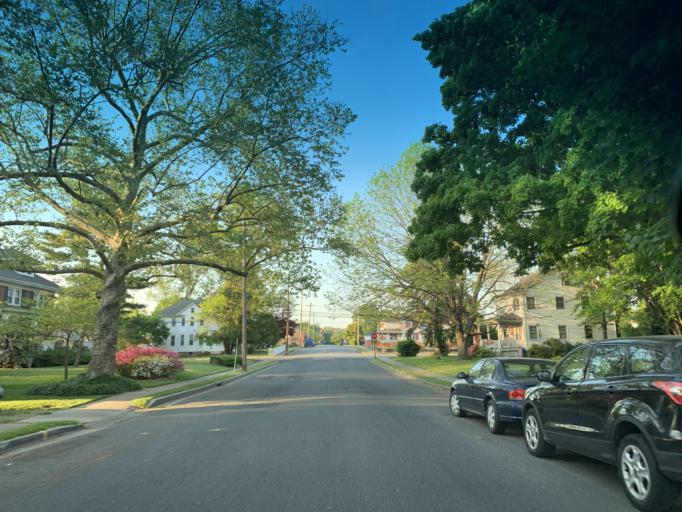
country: US
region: Maryland
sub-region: Harford County
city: Aberdeen
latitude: 39.5087
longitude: -76.1679
